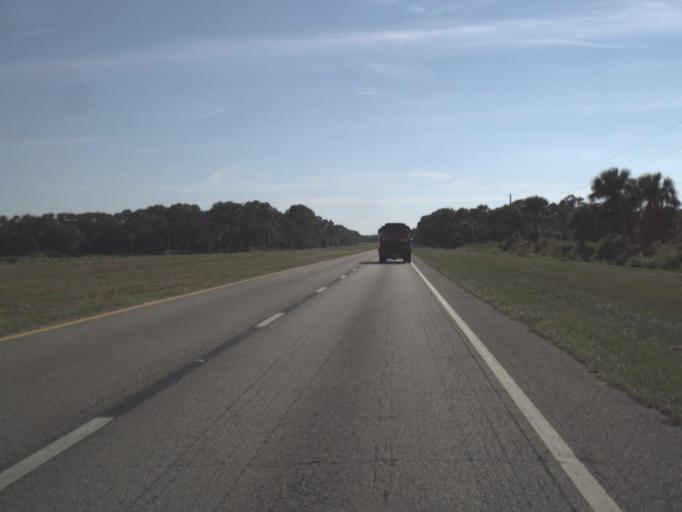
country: US
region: Florida
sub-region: Highlands County
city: Placid Lakes
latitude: 27.0469
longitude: -81.3406
